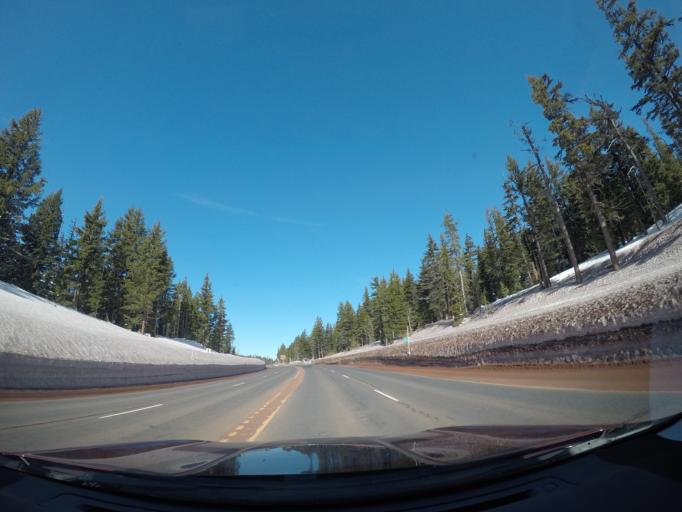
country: US
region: Oregon
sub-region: Deschutes County
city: Sunriver
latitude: 43.9891
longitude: -121.6505
